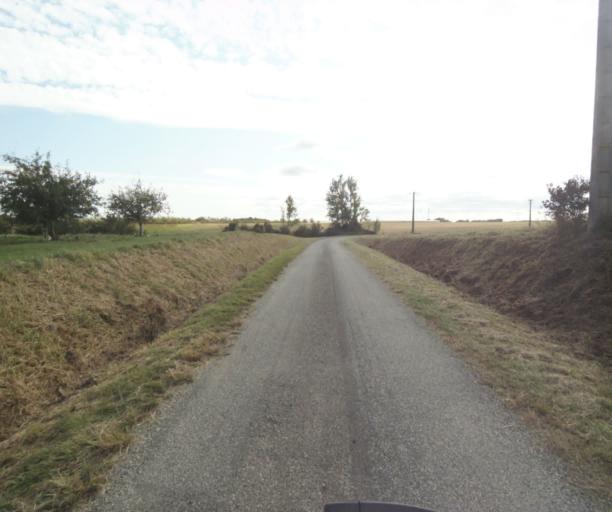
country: FR
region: Midi-Pyrenees
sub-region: Departement du Tarn-et-Garonne
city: Finhan
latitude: 43.8767
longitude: 1.1871
